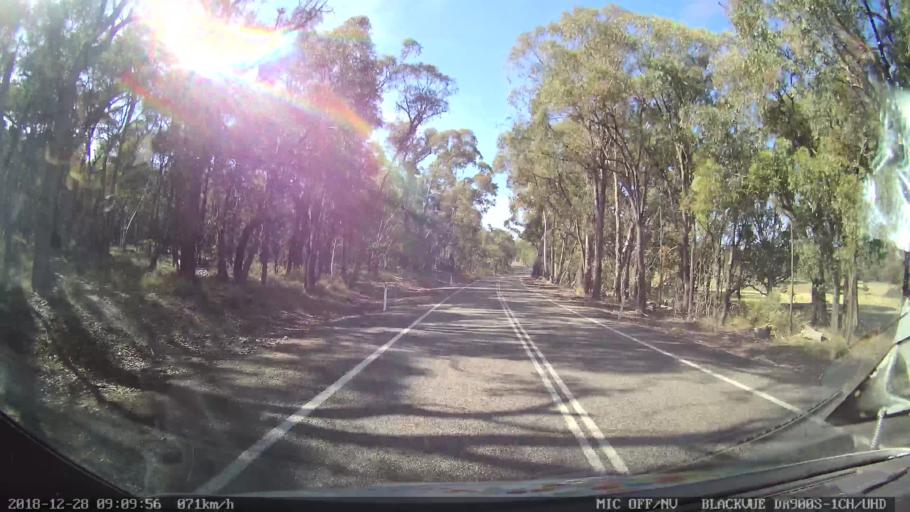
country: AU
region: New South Wales
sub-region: Upper Lachlan Shire
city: Crookwell
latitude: -34.2265
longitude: 149.3360
